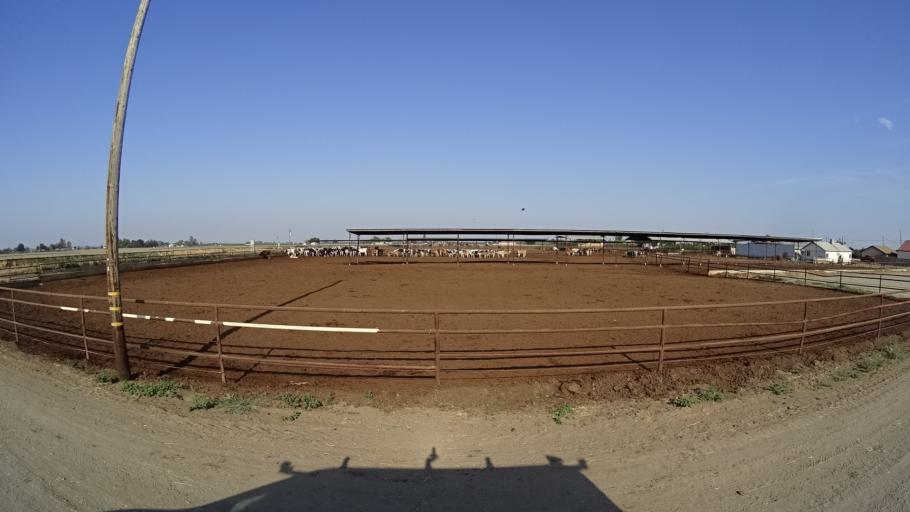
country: US
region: California
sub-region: Fresno County
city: Riverdale
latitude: 36.3792
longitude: -119.8430
